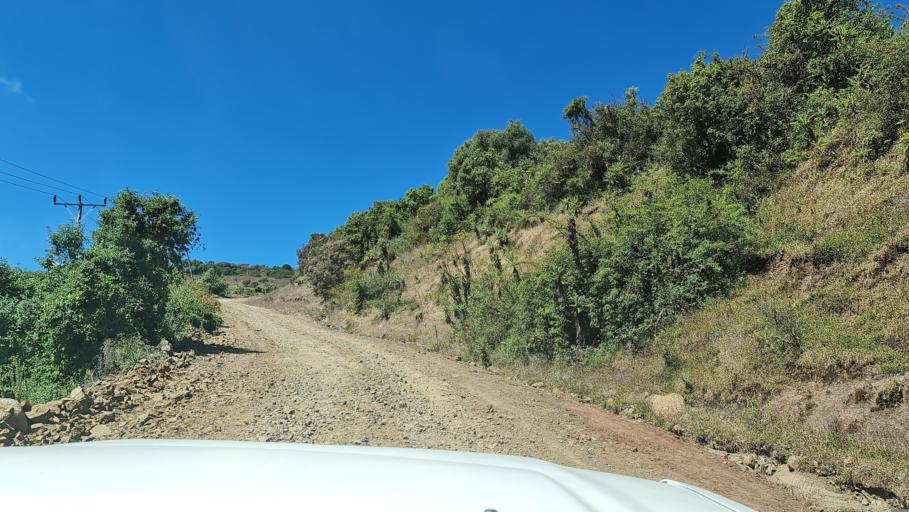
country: ET
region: Amhara
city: Debark'
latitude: 13.2354
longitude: 38.0532
